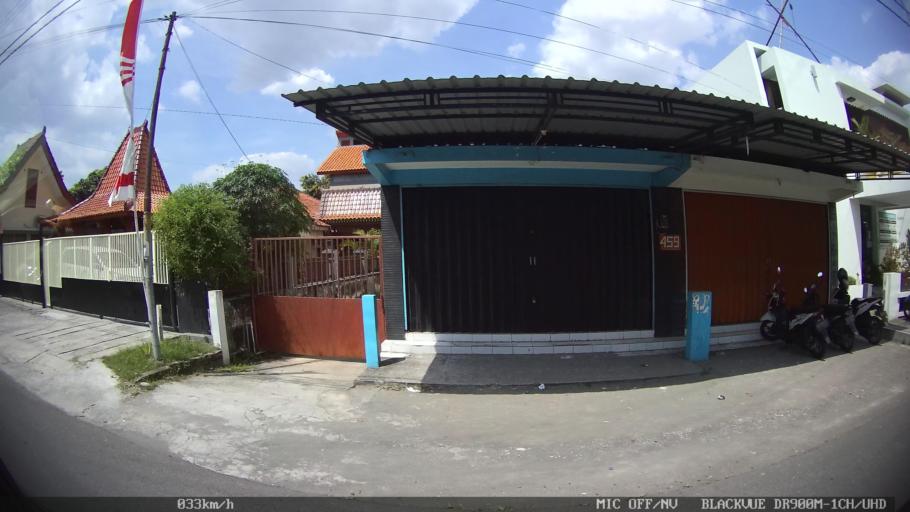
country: ID
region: Daerah Istimewa Yogyakarta
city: Gamping Lor
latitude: -7.8079
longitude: 110.3406
